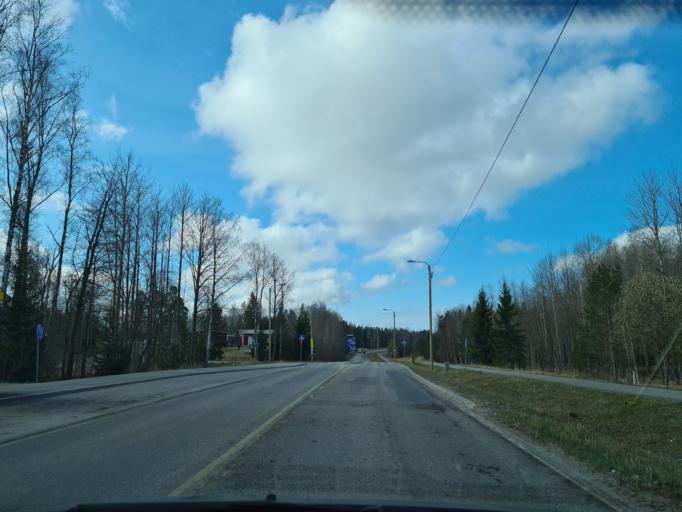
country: FI
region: Uusimaa
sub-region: Helsinki
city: Kirkkonummi
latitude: 60.0810
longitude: 24.4006
